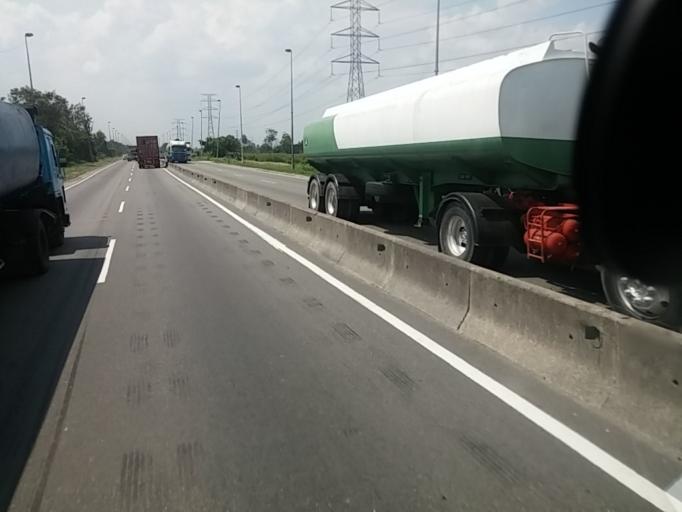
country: MY
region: Selangor
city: Klang
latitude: 2.9742
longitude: 101.3669
